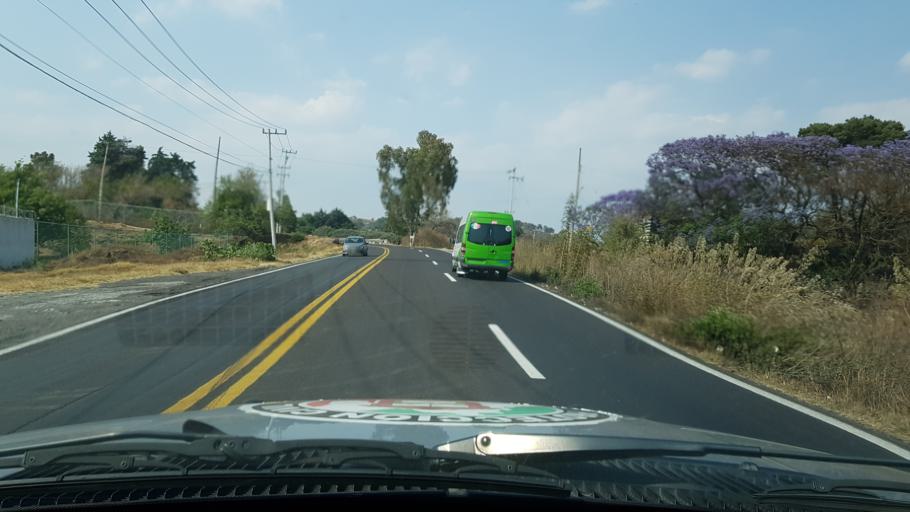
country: MX
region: Mexico
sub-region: Ozumba
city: San Jose Tlacotitlan
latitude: 19.0035
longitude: -98.8212
